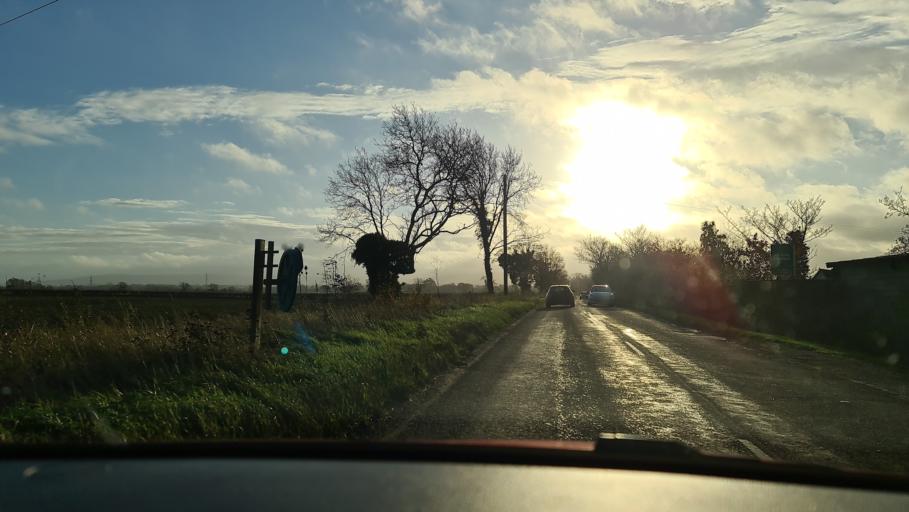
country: GB
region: England
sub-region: Buckinghamshire
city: Stone
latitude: 51.7960
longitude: -0.8523
